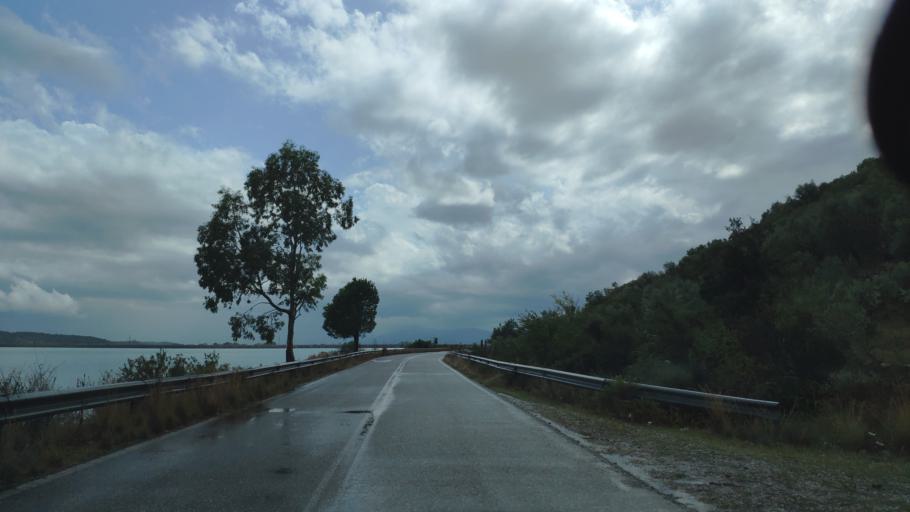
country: GR
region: West Greece
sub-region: Nomos Aitolias kai Akarnanias
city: Lepenou
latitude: 38.6877
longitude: 21.3228
